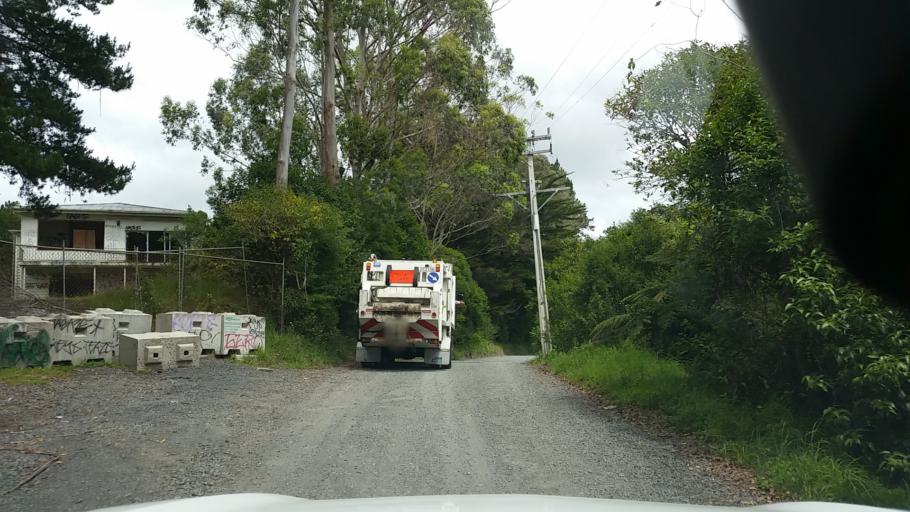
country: NZ
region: Auckland
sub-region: Auckland
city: Rosebank
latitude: -36.8513
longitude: 174.5925
